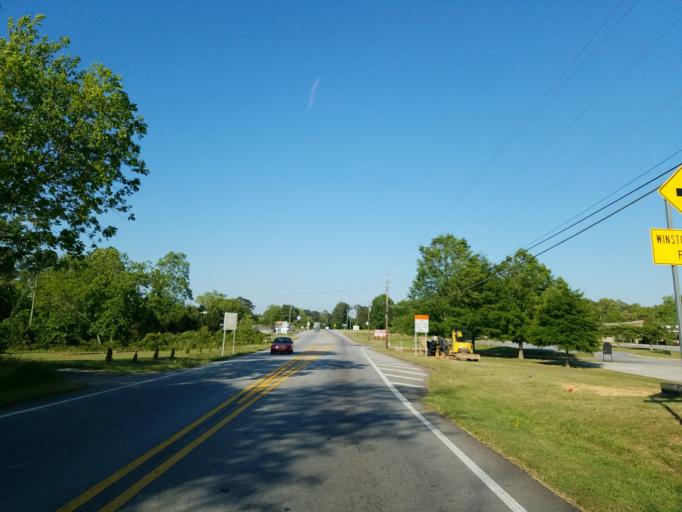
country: US
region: Georgia
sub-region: Douglas County
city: Douglasville
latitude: 33.7284
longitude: -84.8211
